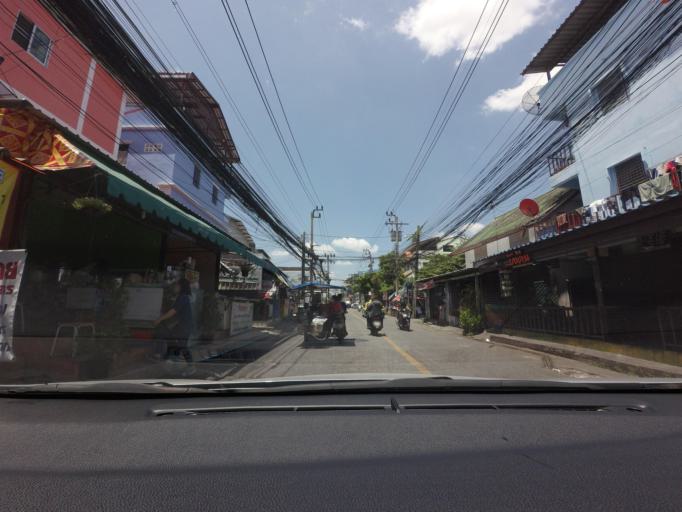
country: TH
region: Bangkok
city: Bang Na
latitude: 13.6913
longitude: 100.6397
